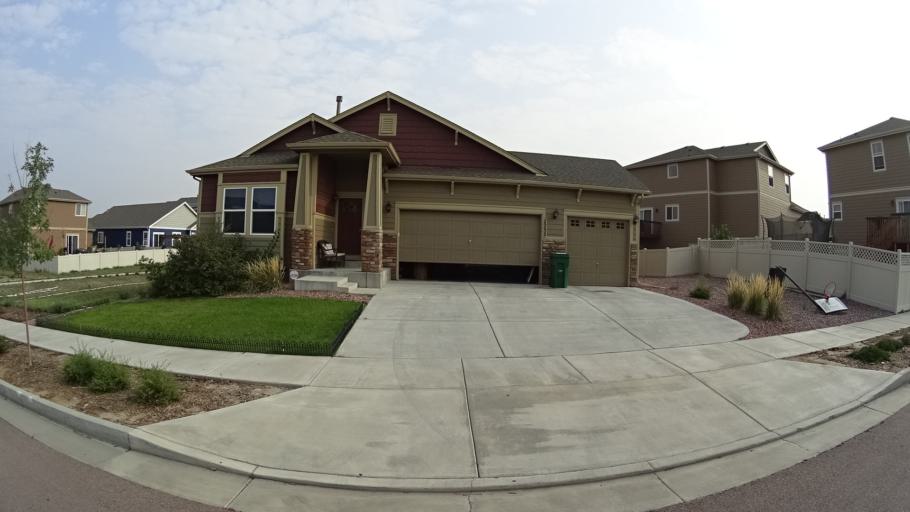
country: US
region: Colorado
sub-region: El Paso County
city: Stratmoor
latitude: 38.8130
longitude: -104.7854
